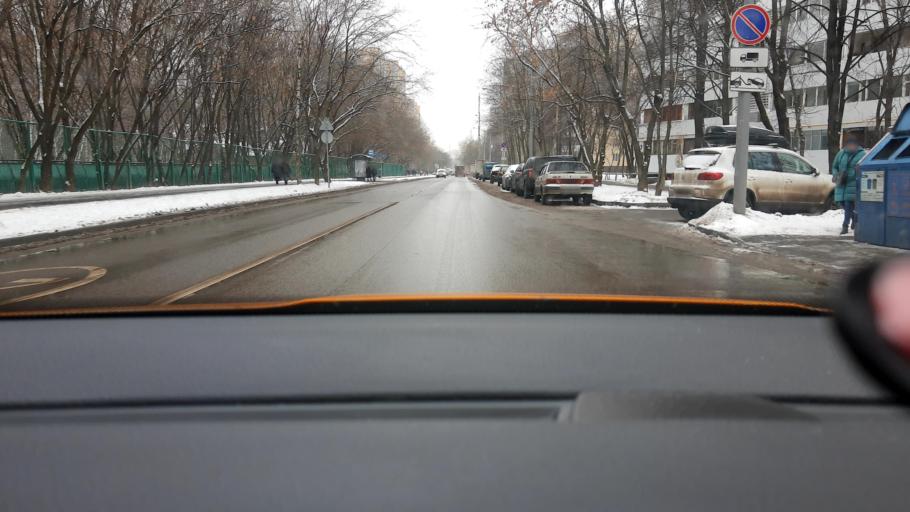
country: RU
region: Moscow
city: Vatutino
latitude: 55.8801
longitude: 37.7019
